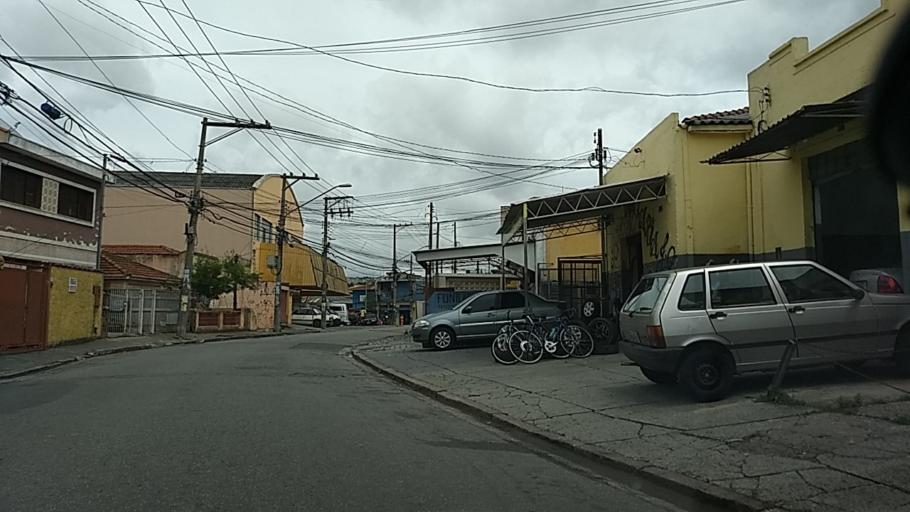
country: BR
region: Sao Paulo
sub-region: Guarulhos
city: Guarulhos
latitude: -23.4804
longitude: -46.5892
